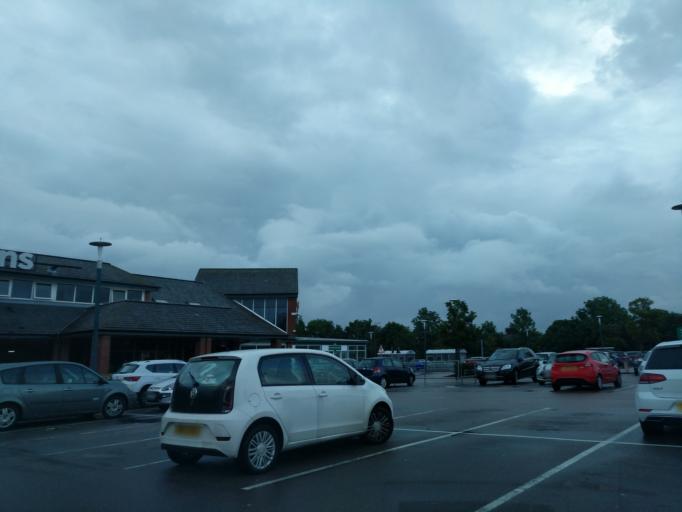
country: GB
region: England
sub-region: Nottinghamshire
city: West Bridgford
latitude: 52.9241
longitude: -1.1024
